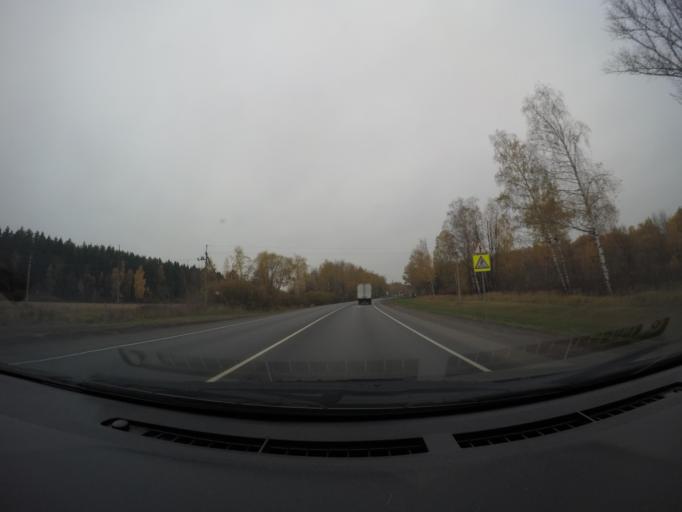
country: RU
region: Moskovskaya
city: Bronnitsy
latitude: 55.3767
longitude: 38.1718
